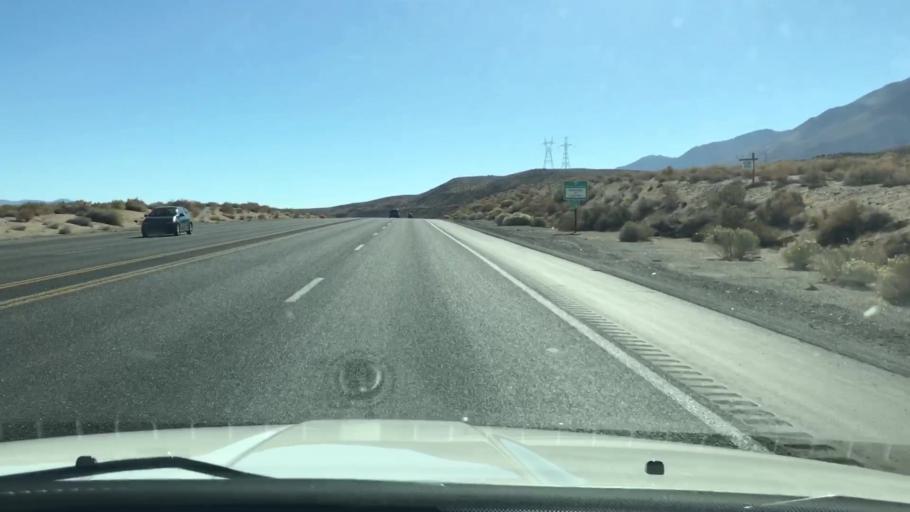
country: US
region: California
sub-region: Inyo County
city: Lone Pine
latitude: 36.5346
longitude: -118.0459
